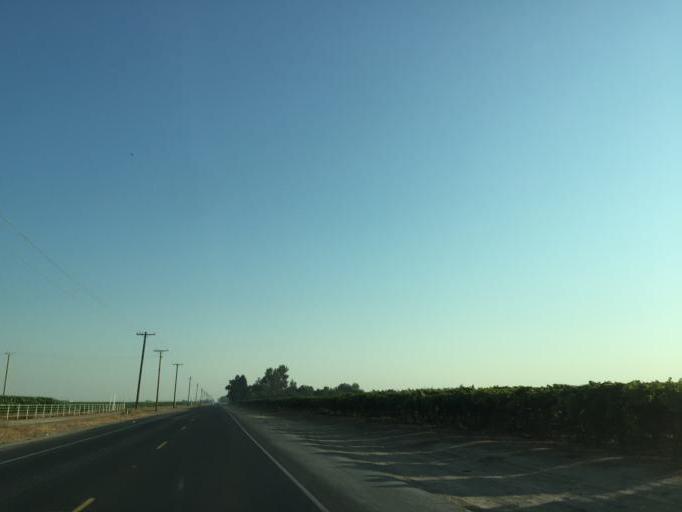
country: US
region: California
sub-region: Tulare County
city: Ivanhoe
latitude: 36.4181
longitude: -119.2961
